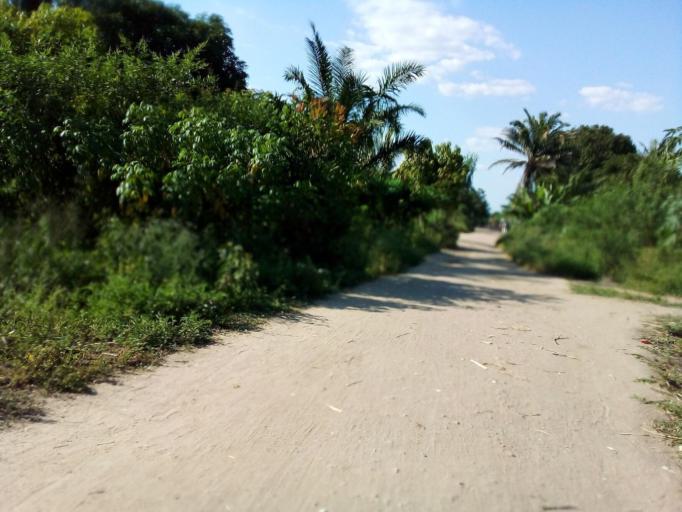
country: MZ
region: Zambezia
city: Quelimane
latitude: -17.5981
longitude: 36.8275
